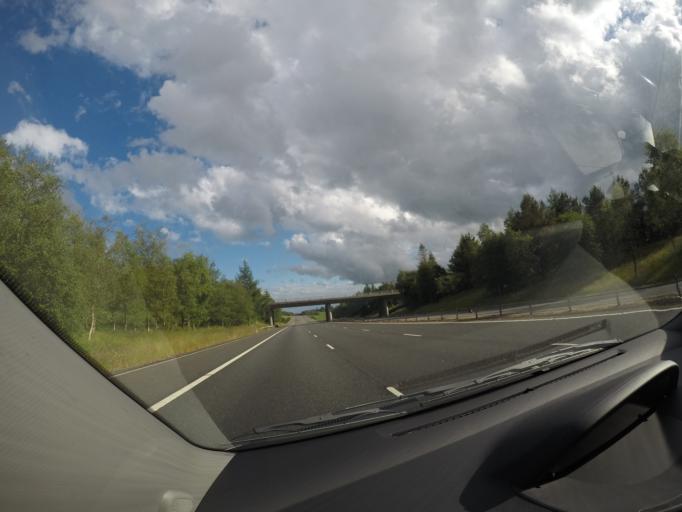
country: GB
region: Scotland
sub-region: Dumfries and Galloway
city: Lockerbie
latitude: 55.1341
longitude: -3.3692
